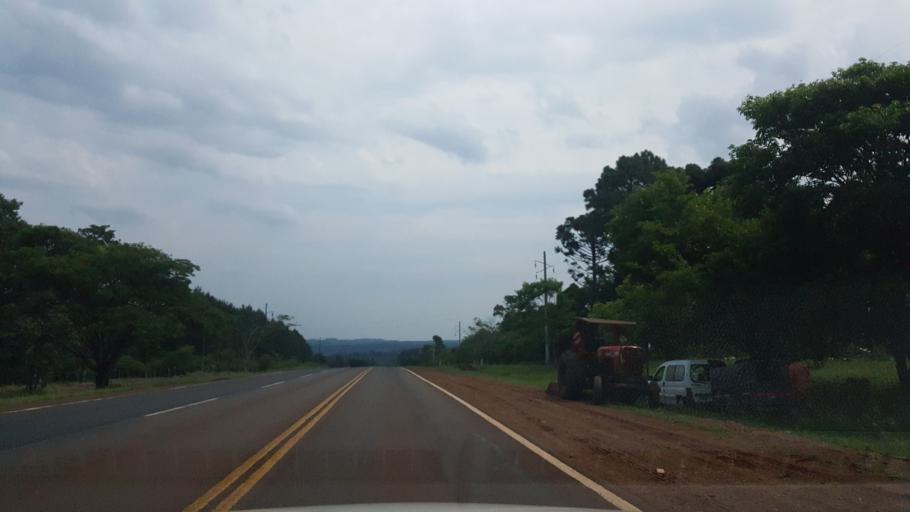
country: AR
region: Misiones
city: Capiovi
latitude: -26.9477
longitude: -55.0886
